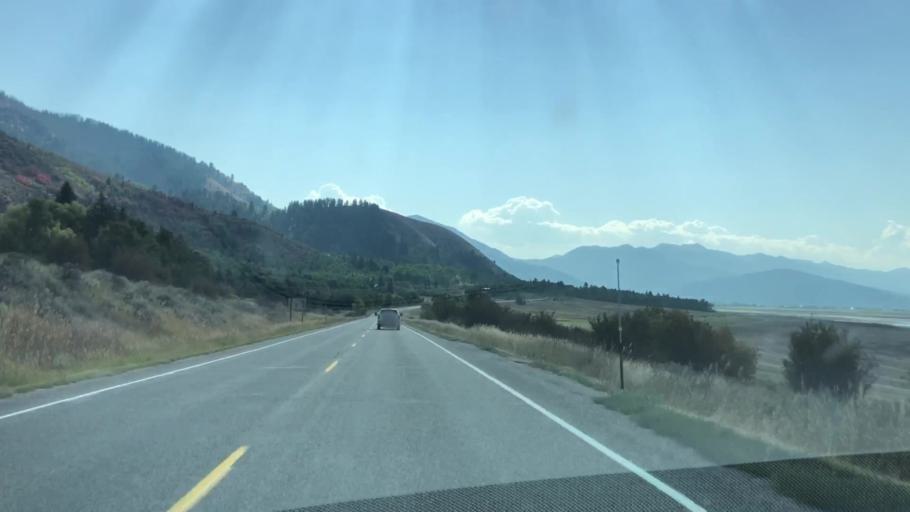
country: US
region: Wyoming
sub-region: Teton County
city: Hoback
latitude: 43.2185
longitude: -111.0694
